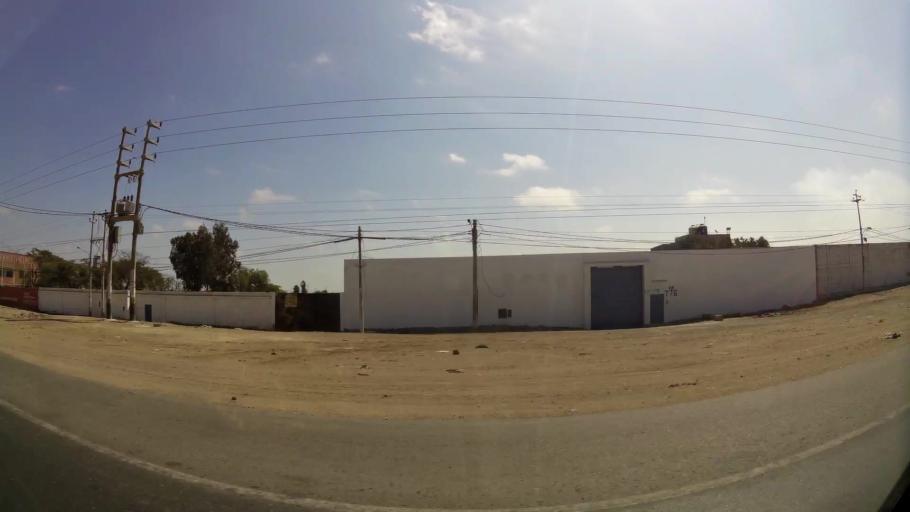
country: PE
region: Lambayeque
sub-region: Provincia de Chiclayo
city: Reque
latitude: -6.8207
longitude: -79.8295
